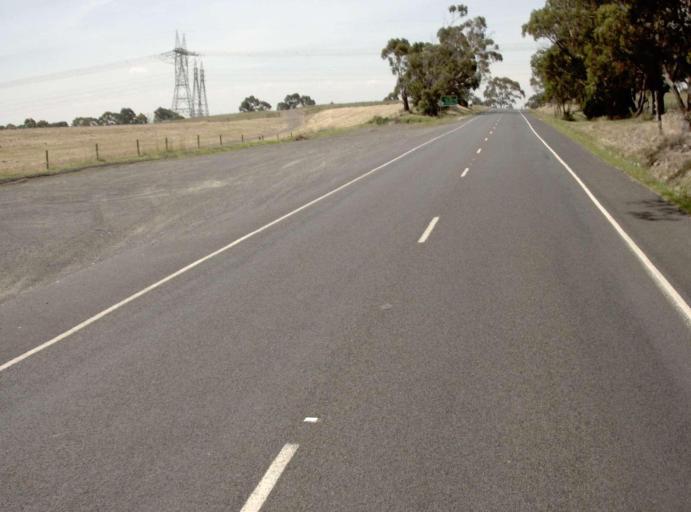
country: AU
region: Victoria
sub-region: Latrobe
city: Traralgon
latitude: -38.2537
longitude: 146.5502
